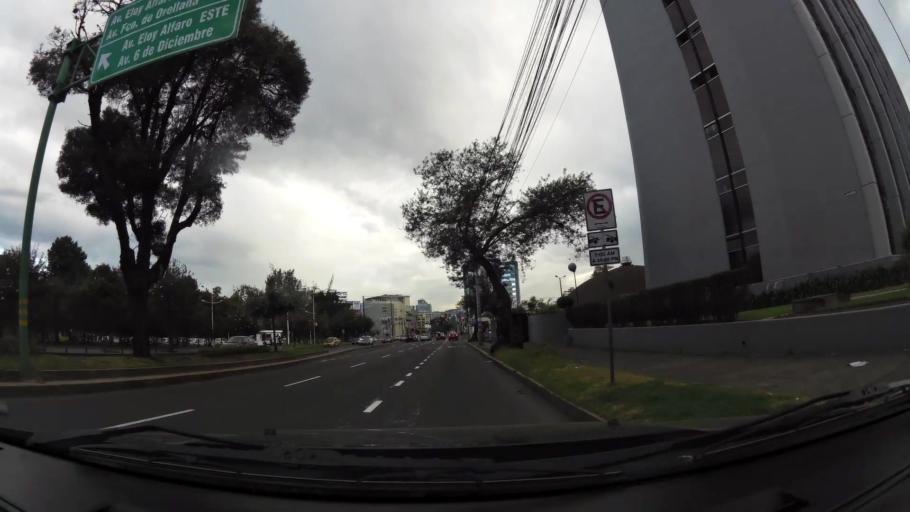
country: EC
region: Pichincha
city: Quito
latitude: -0.1864
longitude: -78.4874
